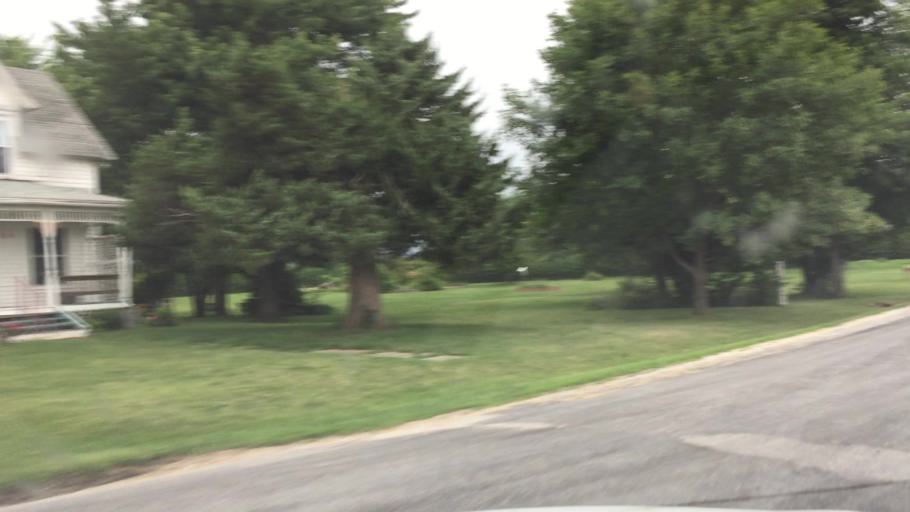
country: US
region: Illinois
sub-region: Adams County
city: Camp Point
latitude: 40.2157
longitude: -90.9693
